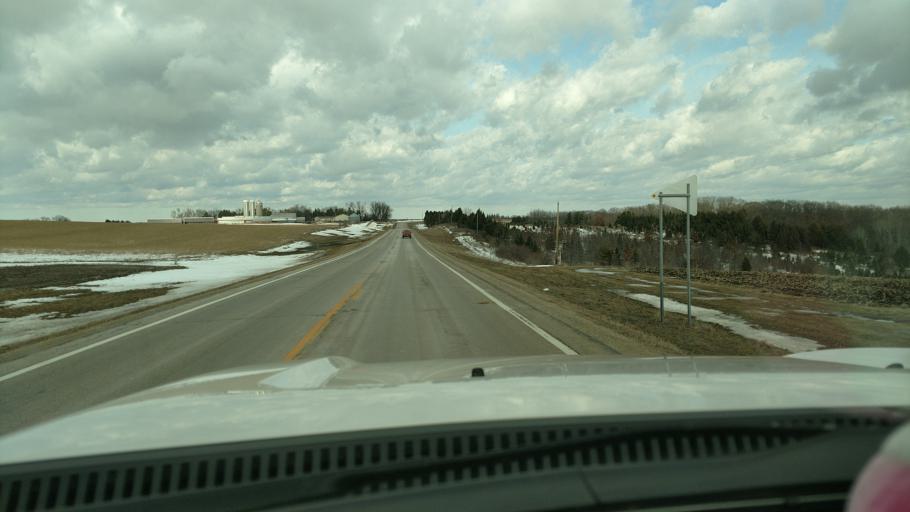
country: US
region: Minnesota
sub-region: Wabasha County
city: Wabasha
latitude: 44.2536
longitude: -92.0533
